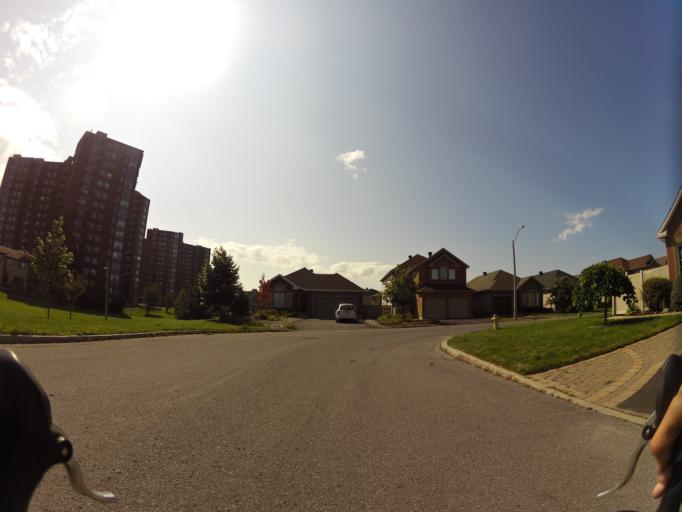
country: CA
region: Ontario
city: Ottawa
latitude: 45.3772
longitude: -75.6555
